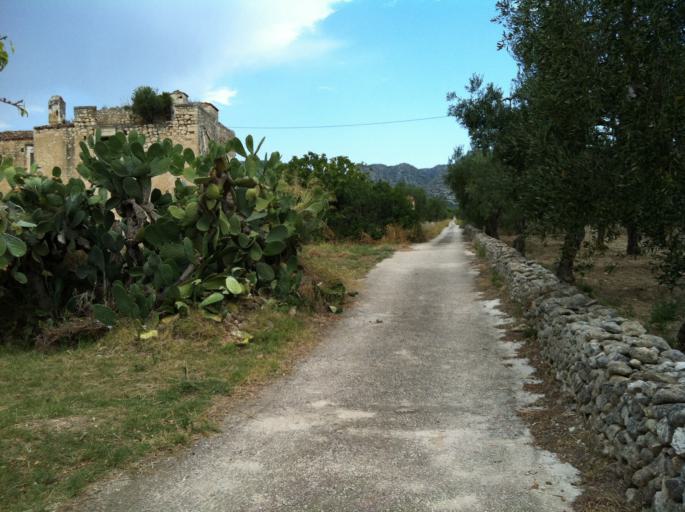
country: IT
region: Apulia
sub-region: Provincia di Foggia
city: Monte Sant'Angelo
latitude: 41.6543
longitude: 15.9560
